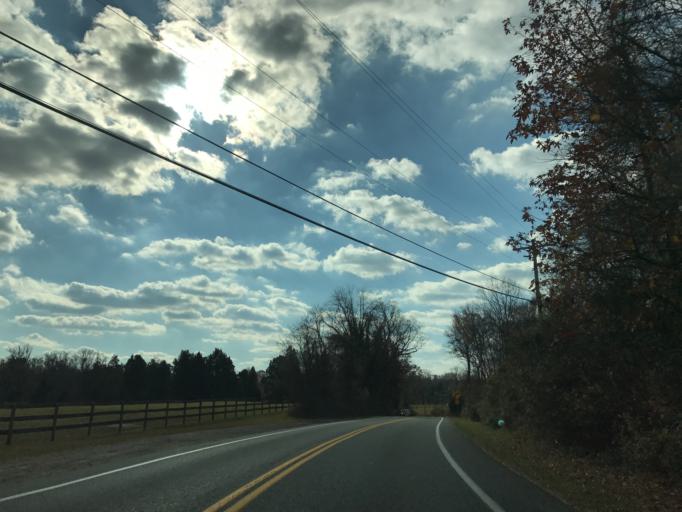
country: US
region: Maryland
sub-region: Harford County
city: Pleasant Hills
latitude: 39.4810
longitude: -76.3742
